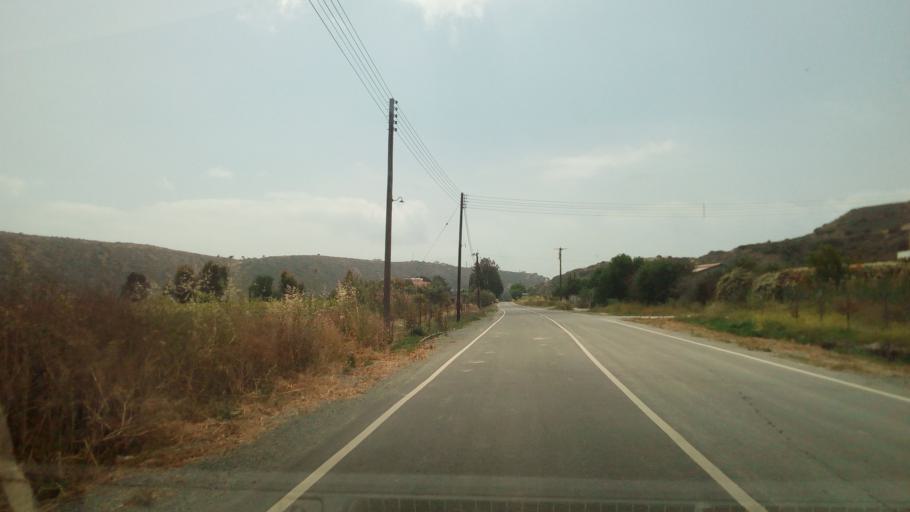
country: CY
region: Limassol
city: Pissouri
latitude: 34.6687
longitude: 32.7263
